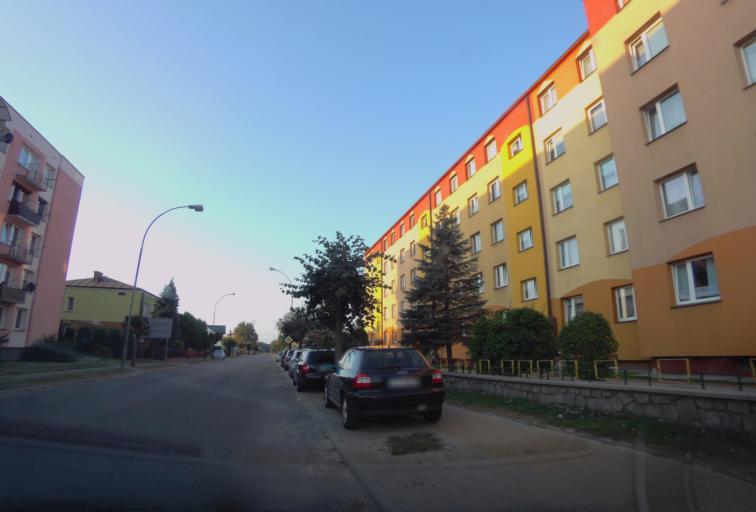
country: PL
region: Lublin Voivodeship
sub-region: Powiat janowski
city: Janow Lubelski
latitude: 50.6995
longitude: 22.4205
